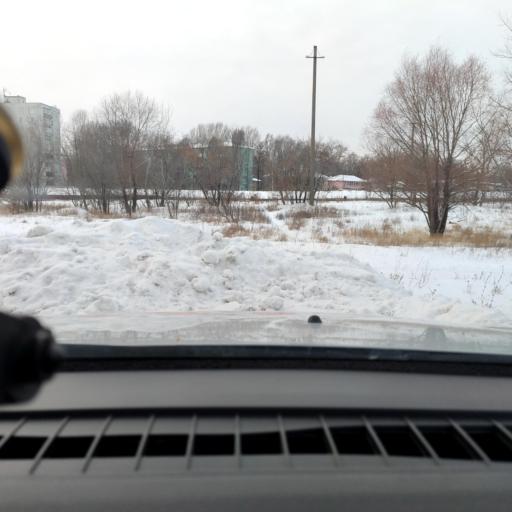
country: RU
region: Samara
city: Samara
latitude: 53.1109
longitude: 50.0842
